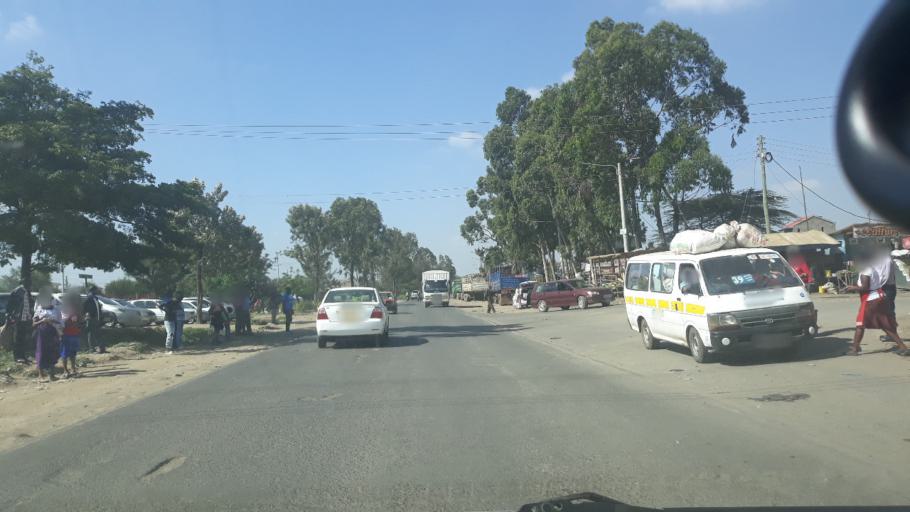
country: KE
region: Nairobi Area
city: Pumwani
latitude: -1.2709
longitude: 36.9000
